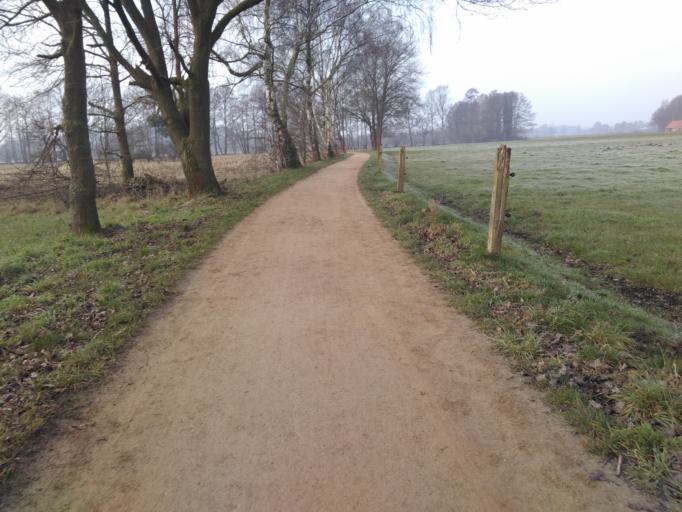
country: DE
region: North Rhine-Westphalia
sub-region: Regierungsbezirk Detmold
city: Verl
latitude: 51.8885
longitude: 8.4778
